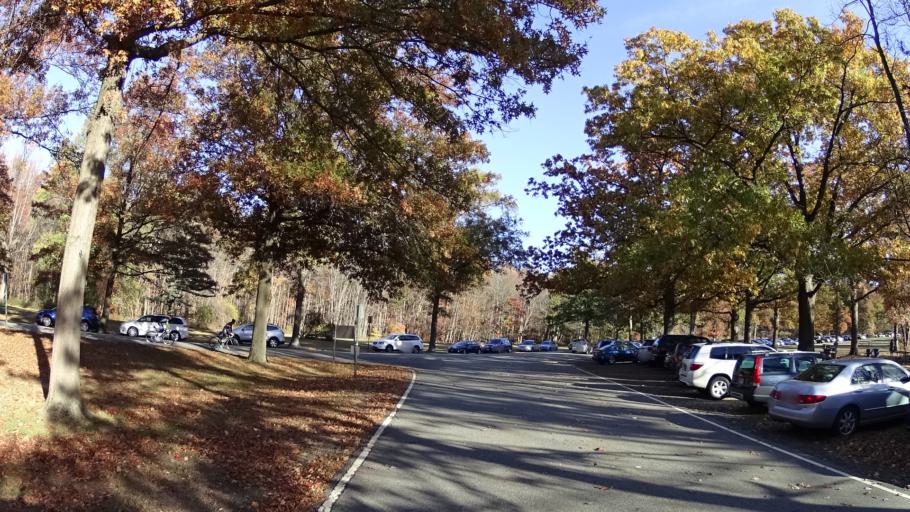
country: US
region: New Jersey
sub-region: Union County
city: Mountainside
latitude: 40.6878
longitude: -74.3729
